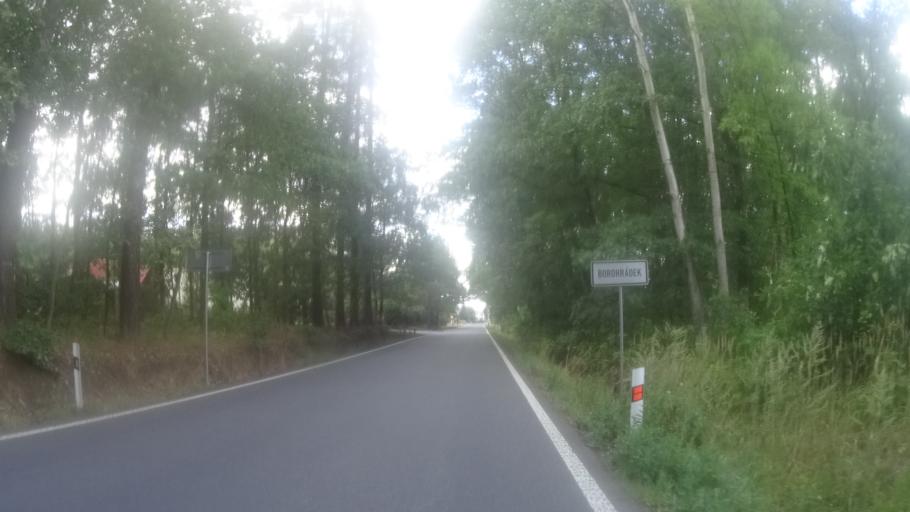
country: CZ
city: Borohradek
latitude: 50.0908
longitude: 16.1038
